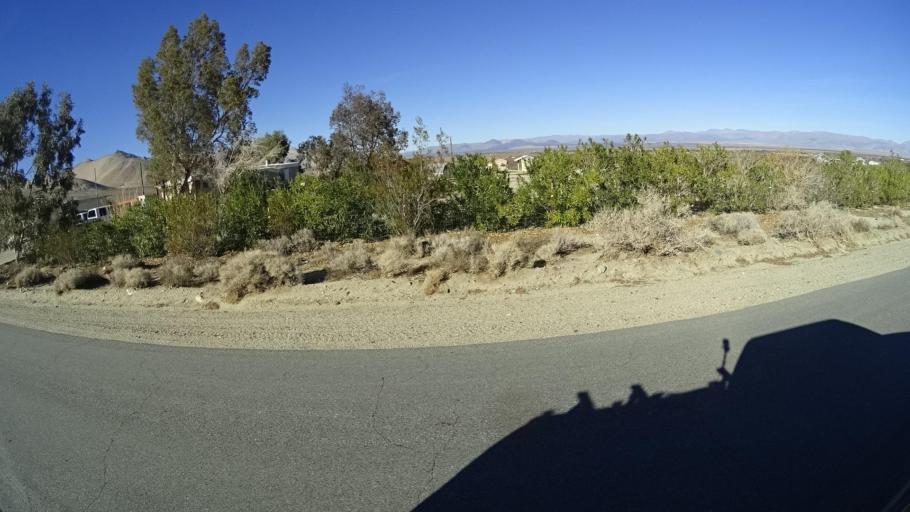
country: US
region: California
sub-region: Kern County
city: Inyokern
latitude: 35.6811
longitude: -117.8609
